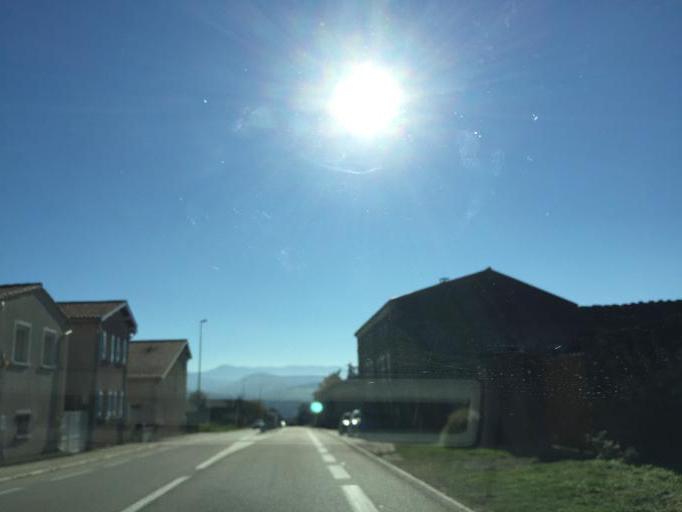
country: FR
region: Rhone-Alpes
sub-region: Departement du Rhone
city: Saint-Maurice-sur-Dargoire
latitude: 45.5596
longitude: 4.6415
